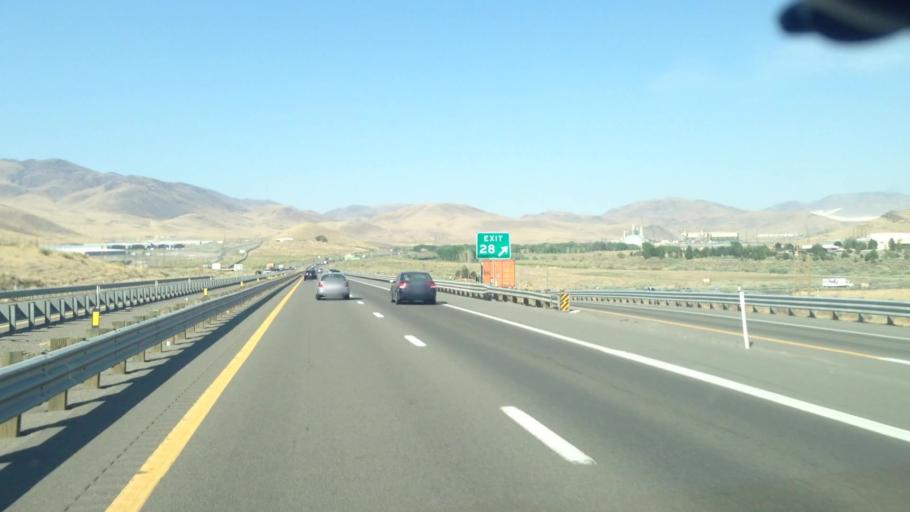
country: US
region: Nevada
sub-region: Washoe County
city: Spanish Springs
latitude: 39.5572
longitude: -119.5585
